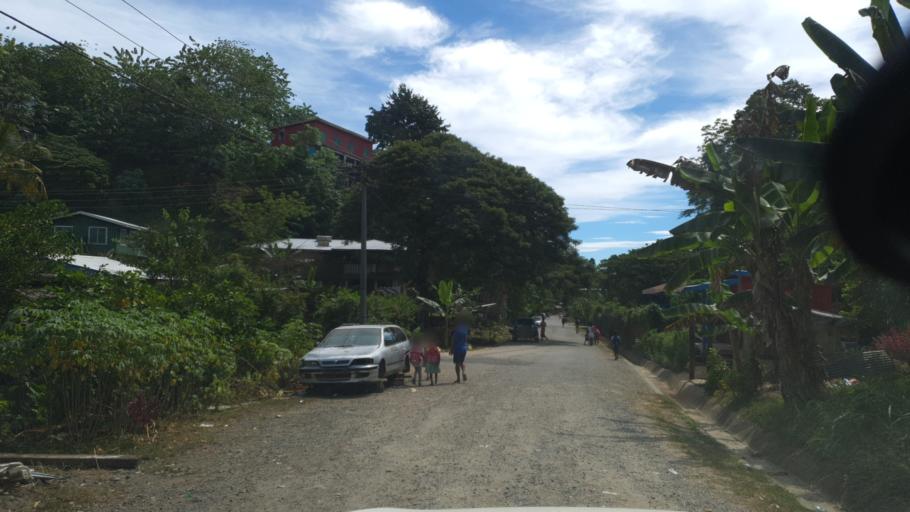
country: SB
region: Guadalcanal
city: Honiara
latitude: -9.4299
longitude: 159.9321
